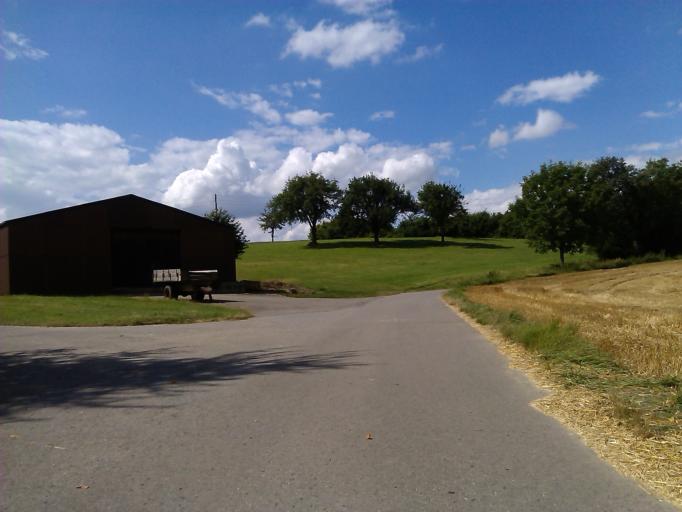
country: DE
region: Baden-Wuerttemberg
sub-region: Karlsruhe Region
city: Sinsheim
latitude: 49.1857
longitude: 8.8591
